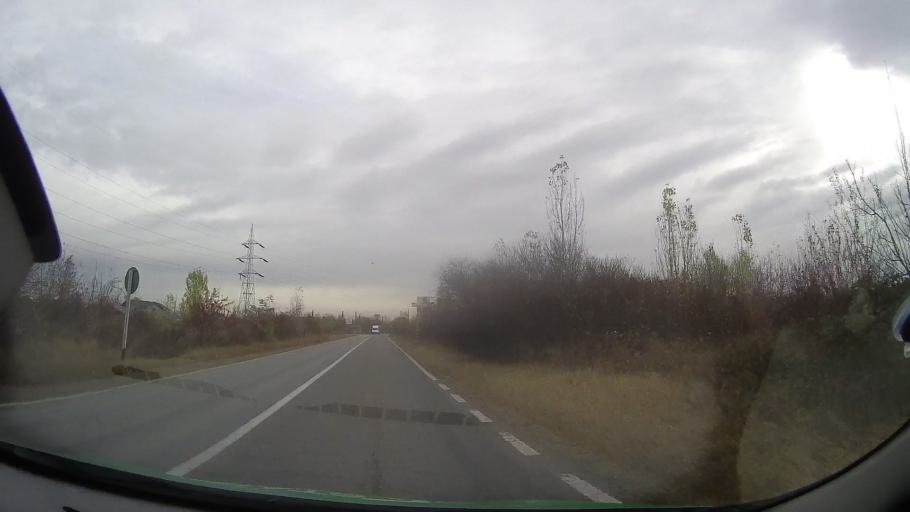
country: RO
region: Prahova
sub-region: Comuna Bucov
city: Bucov
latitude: 44.9497
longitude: 26.0961
